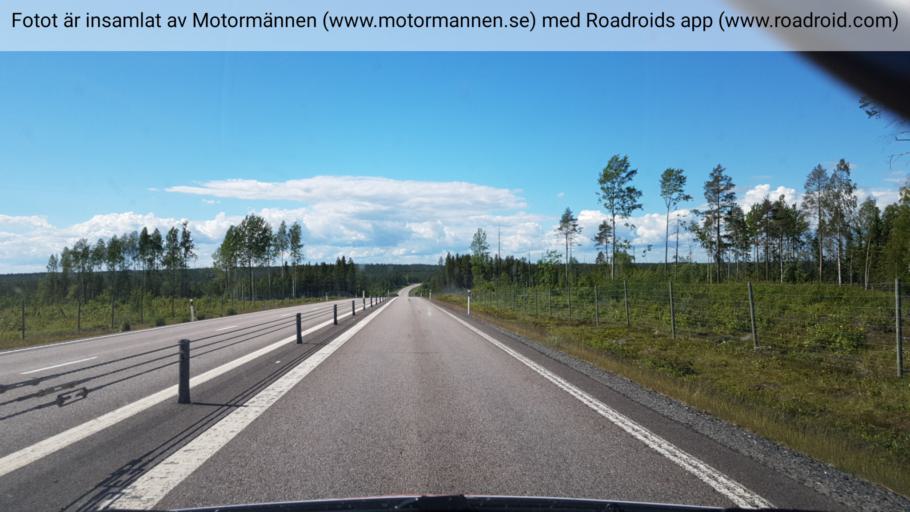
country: SE
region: Norrbotten
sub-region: Kalix Kommun
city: Toere
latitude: 65.9104
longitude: 22.8193
